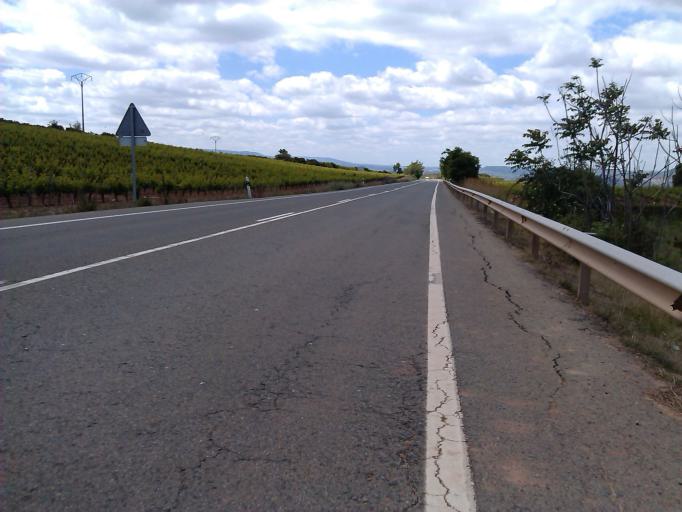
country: ES
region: La Rioja
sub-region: Provincia de La Rioja
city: Manjarres
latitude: 42.4107
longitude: -2.6553
